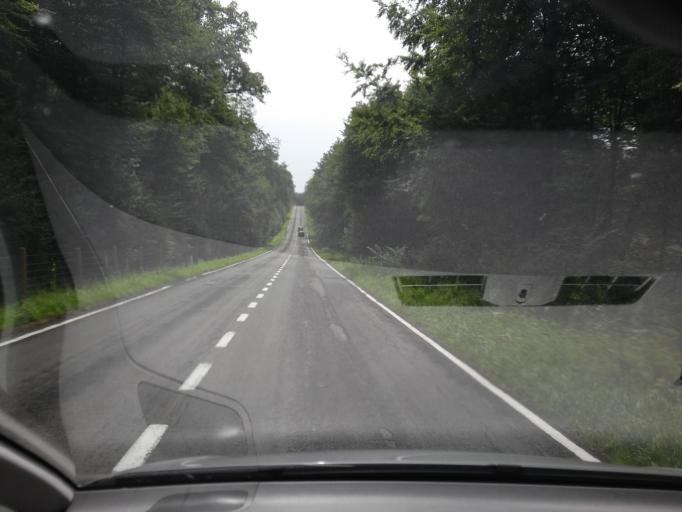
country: BE
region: Wallonia
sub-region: Province du Luxembourg
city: Chiny
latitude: 49.7752
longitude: 5.3518
